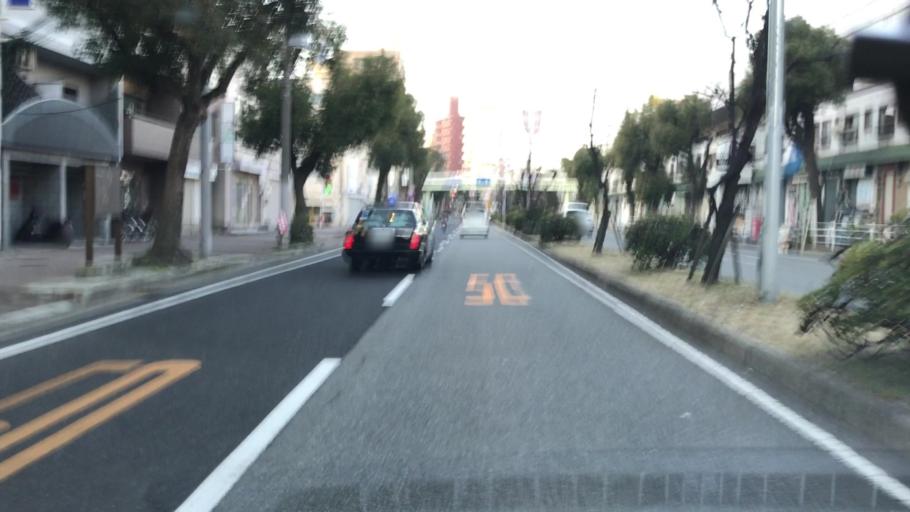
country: JP
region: Hyogo
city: Kobe
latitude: 34.6861
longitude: 135.1819
